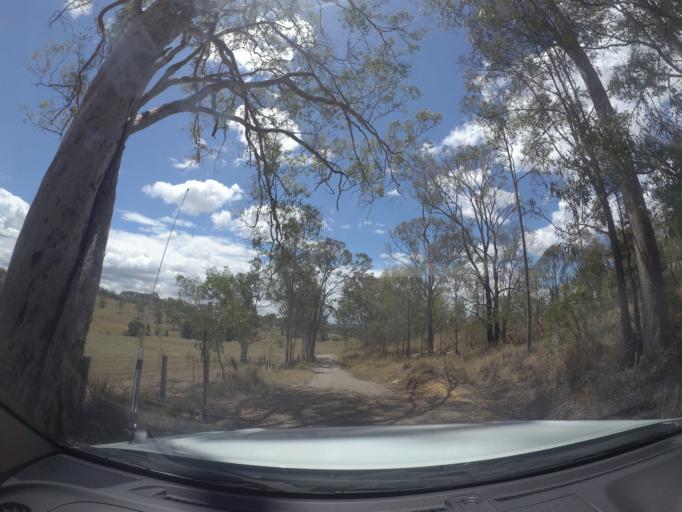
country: AU
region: Queensland
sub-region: Logan
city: Cedar Vale
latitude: -27.9038
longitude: 153.0590
